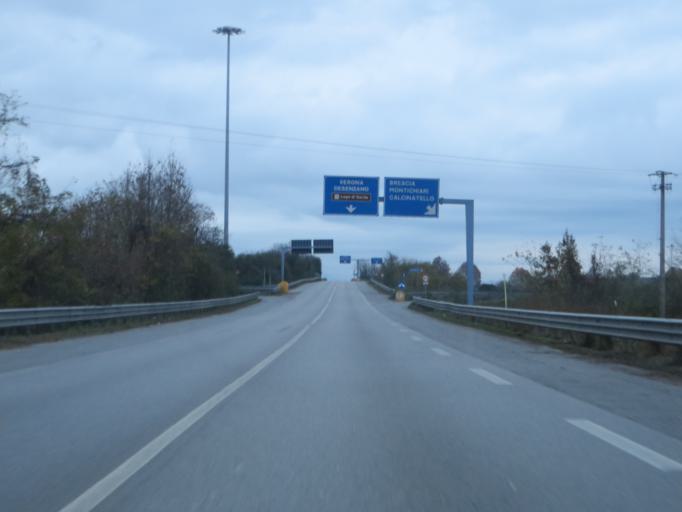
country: IT
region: Lombardy
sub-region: Provincia di Brescia
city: Molinetto
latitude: 45.4827
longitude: 10.3704
